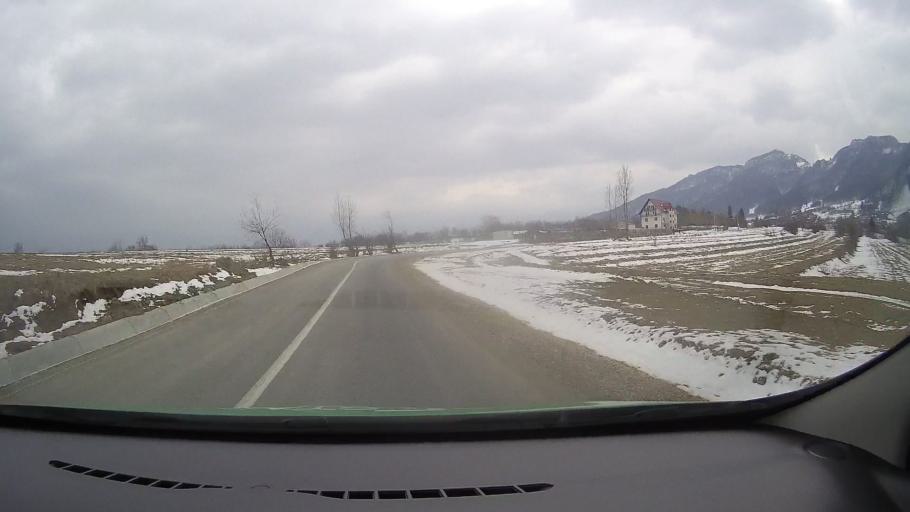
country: RO
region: Brasov
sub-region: Comuna Zarnesti
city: Zarnesti
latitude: 45.5508
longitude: 25.3213
